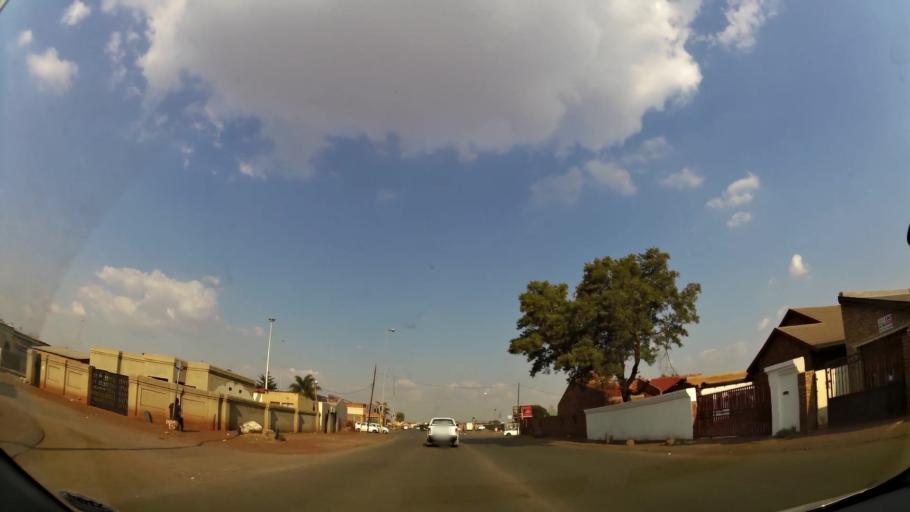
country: ZA
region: Gauteng
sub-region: Ekurhuleni Metropolitan Municipality
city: Germiston
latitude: -26.3581
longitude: 28.1927
